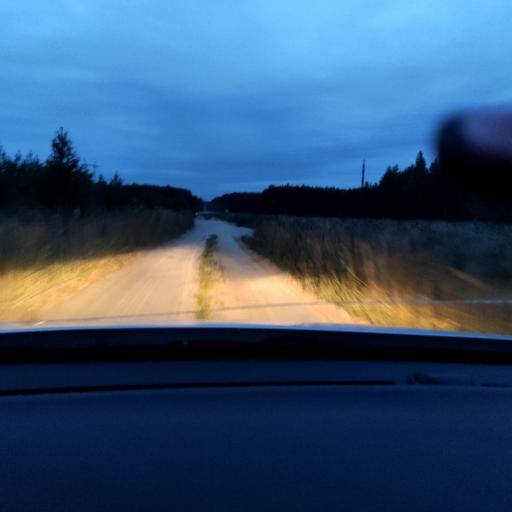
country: RU
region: Mariy-El
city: Volzhsk
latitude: 55.8886
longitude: 48.3973
